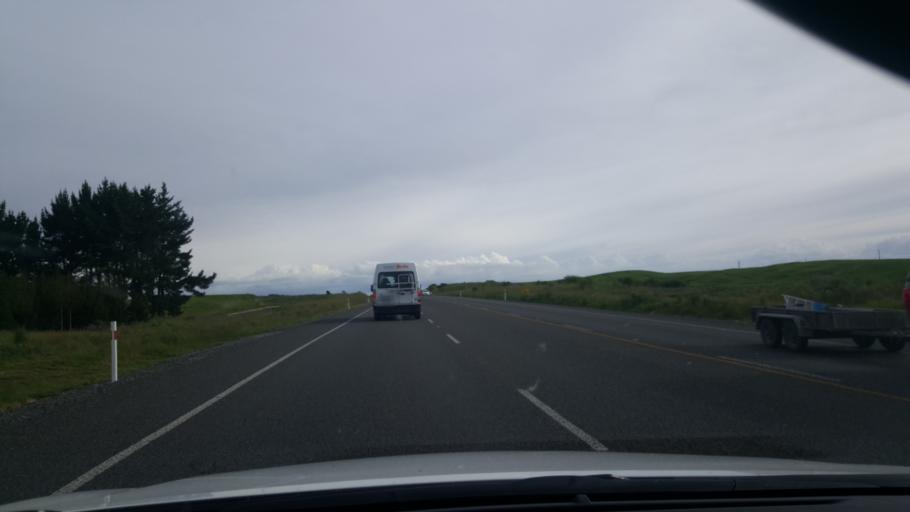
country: NZ
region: Waikato
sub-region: Taupo District
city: Taupo
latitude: -38.6428
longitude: 176.0996
